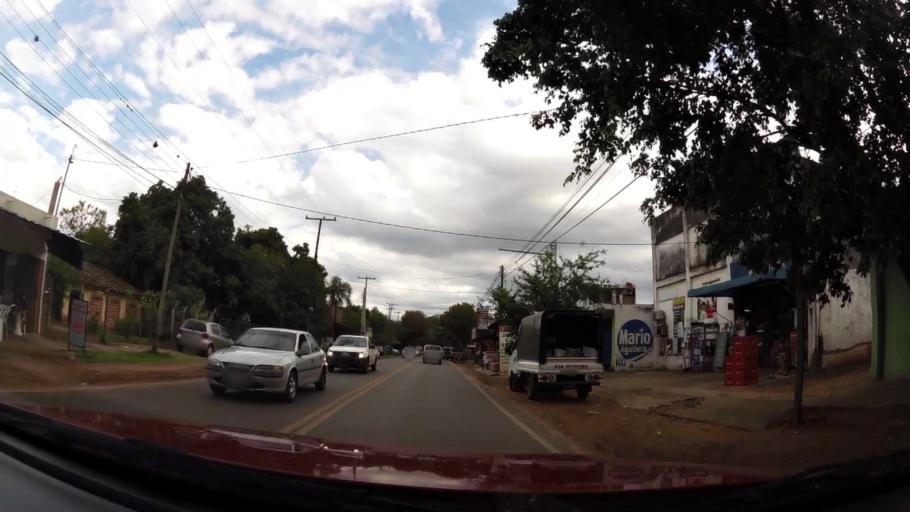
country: PY
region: Central
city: San Lorenzo
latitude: -25.2766
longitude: -57.4858
